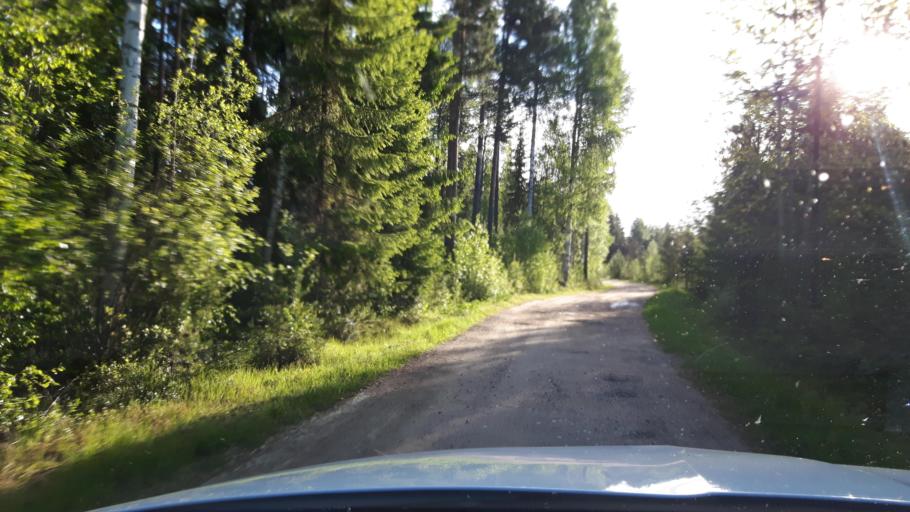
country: SE
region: Gaevleborg
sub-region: Ljusdals Kommun
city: Farila
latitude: 62.0480
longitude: 15.8247
